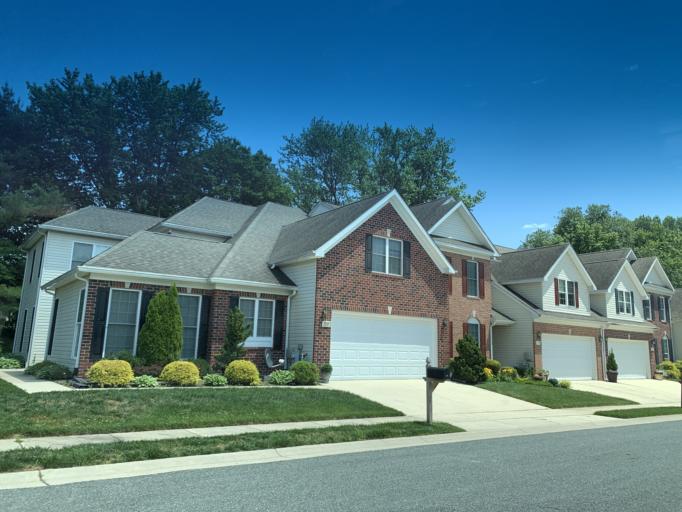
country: US
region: Maryland
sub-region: Harford County
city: Bel Air North
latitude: 39.5743
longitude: -76.3630
